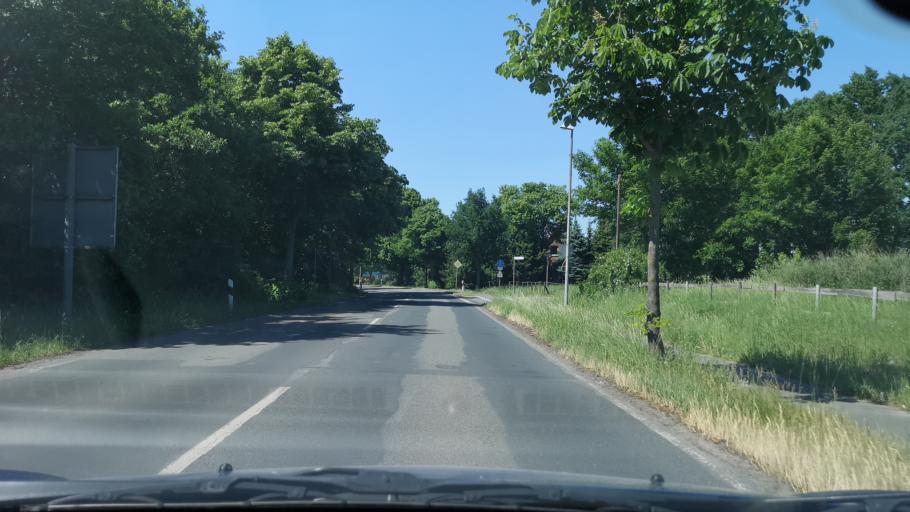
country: DE
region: Lower Saxony
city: Garbsen-Mitte
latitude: 52.4452
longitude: 9.6391
